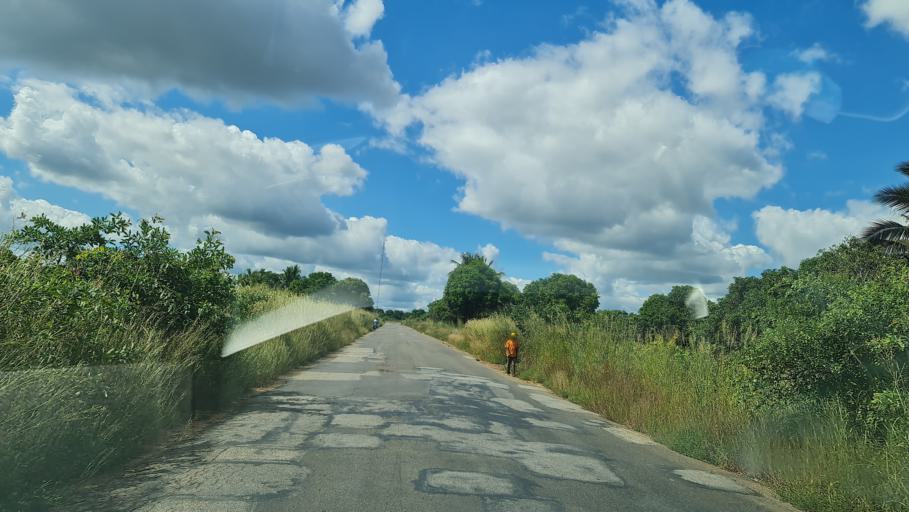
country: MZ
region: Zambezia
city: Quelimane
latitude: -17.5078
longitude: 36.2394
